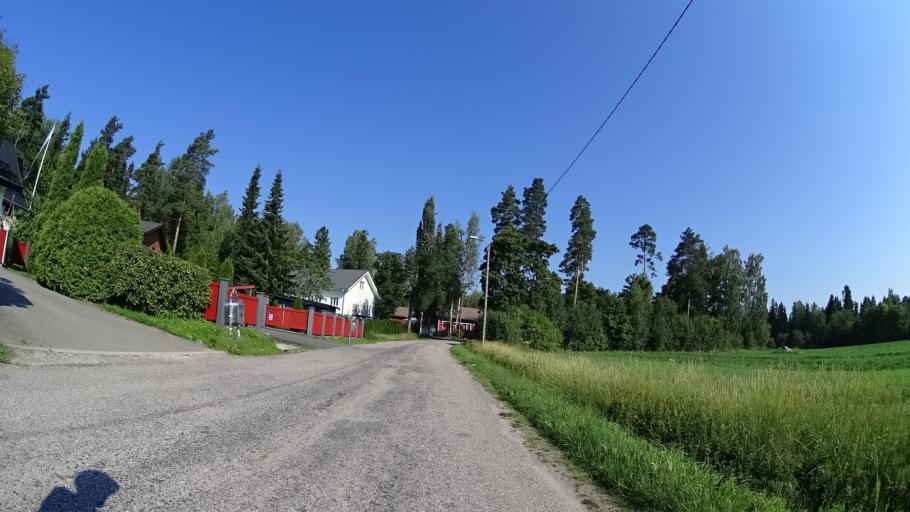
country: FI
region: Uusimaa
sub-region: Helsinki
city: Vantaa
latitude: 60.3167
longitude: 25.0812
